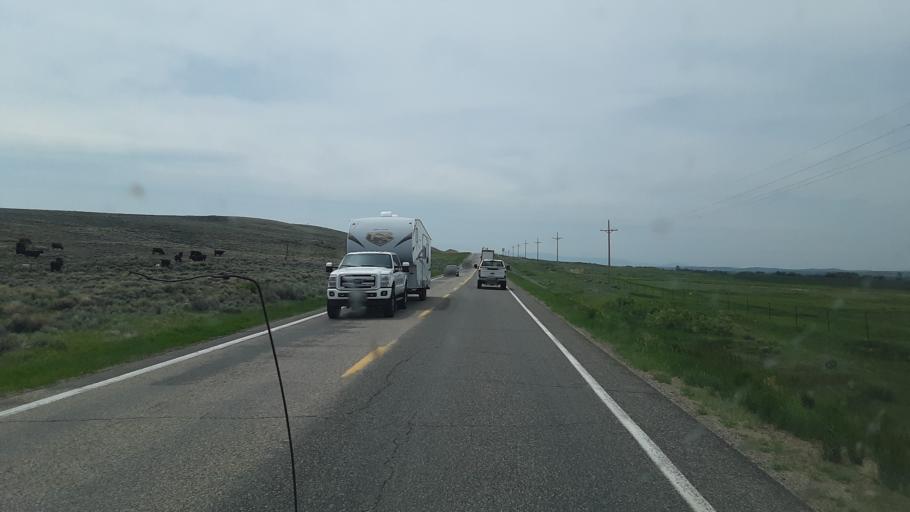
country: US
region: Colorado
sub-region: Jackson County
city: Walden
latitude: 40.7805
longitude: -106.2814
